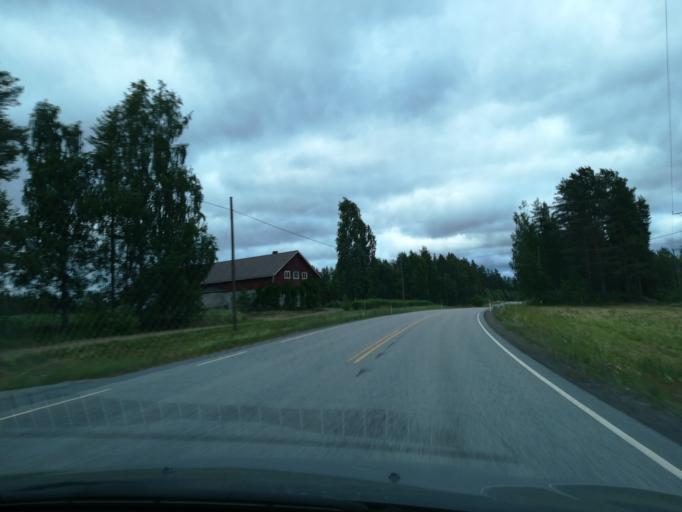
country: FI
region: Southern Savonia
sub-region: Mikkeli
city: Ristiina
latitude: 61.3500
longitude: 27.3794
